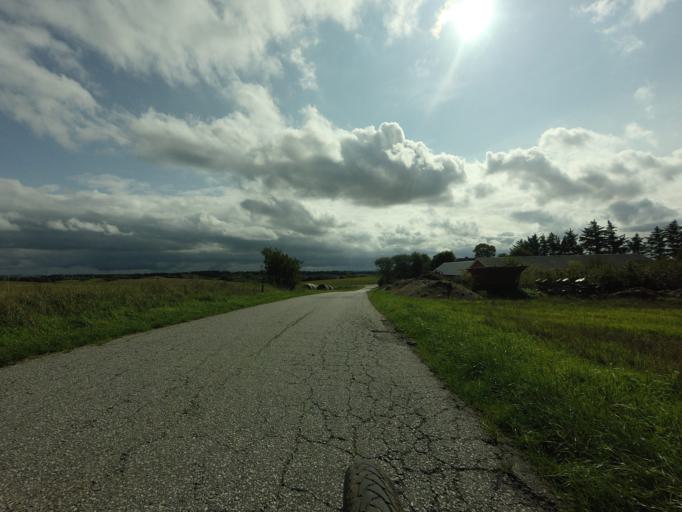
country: DK
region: North Denmark
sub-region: Hjorring Kommune
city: Hjorring
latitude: 57.5308
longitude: 10.0400
